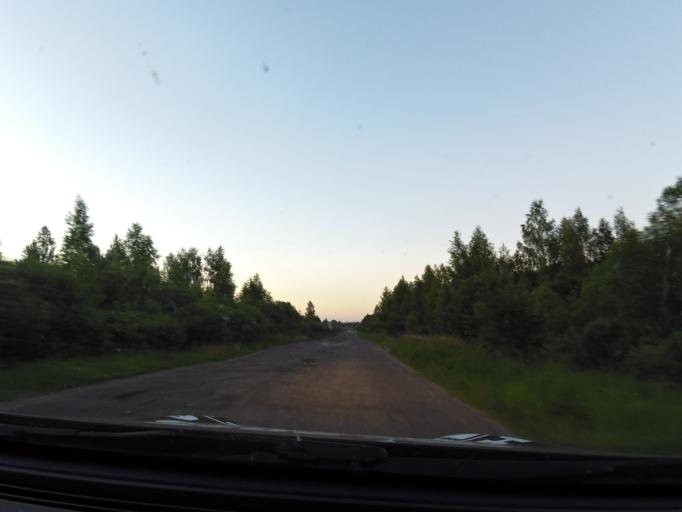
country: RU
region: Kostroma
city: Buy
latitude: 58.4502
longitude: 41.3570
